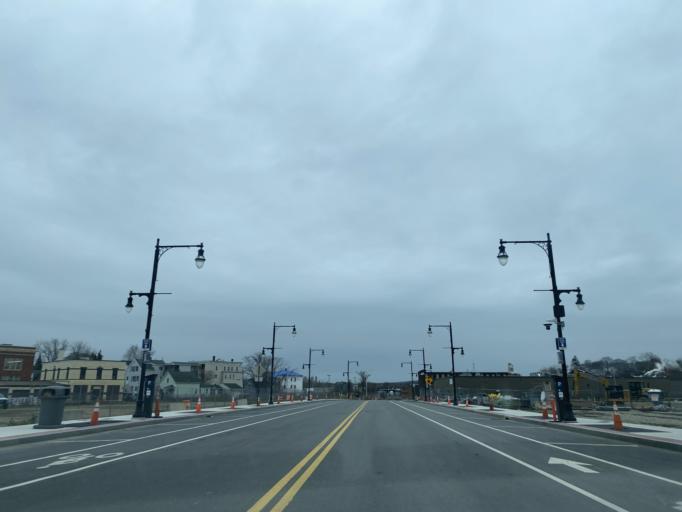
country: US
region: Massachusetts
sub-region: Worcester County
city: Worcester
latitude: 42.2554
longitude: -71.8015
